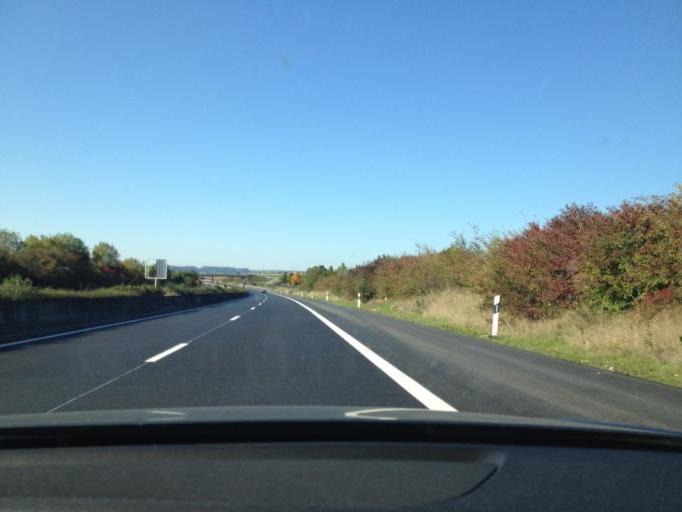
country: LU
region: Grevenmacher
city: Schengen
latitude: 49.4869
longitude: 6.3340
